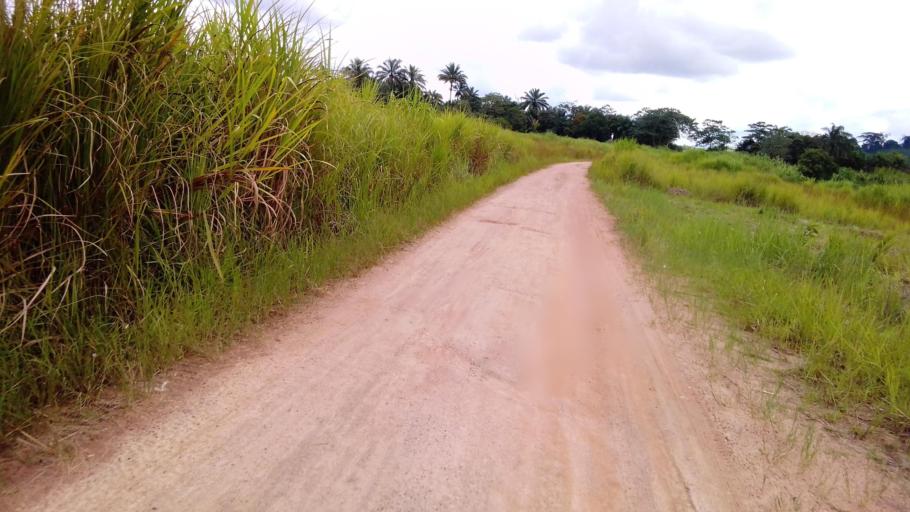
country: SL
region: Eastern Province
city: Koidu
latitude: 8.6808
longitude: -10.9605
